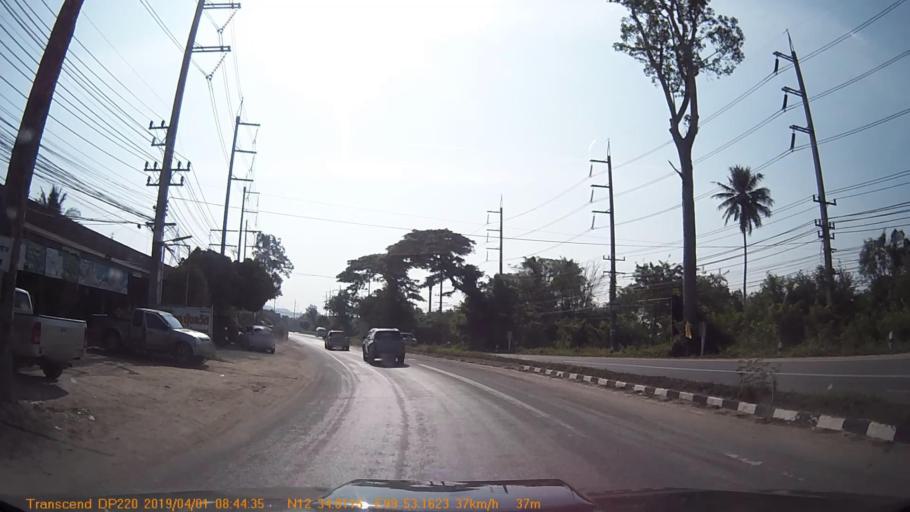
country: TH
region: Prachuap Khiri Khan
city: Hua Hin
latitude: 12.5668
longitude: 99.8863
